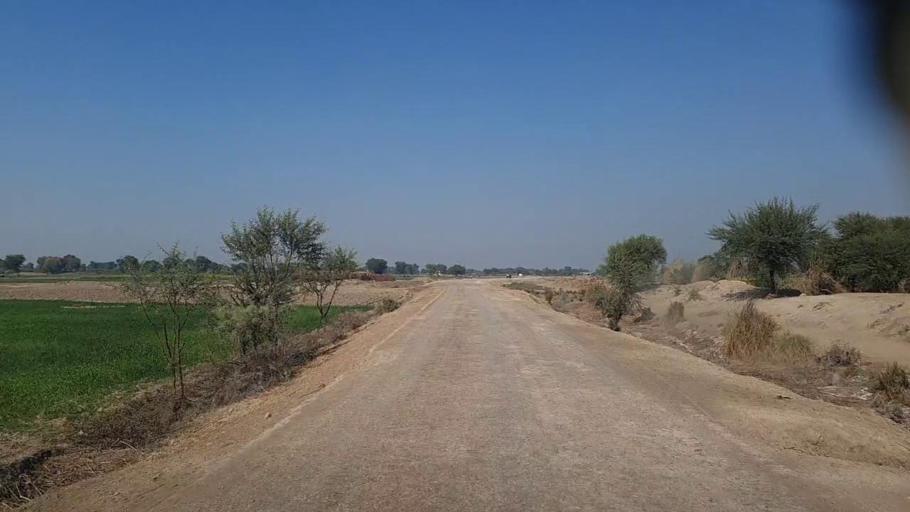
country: PK
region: Sindh
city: Khairpur
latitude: 27.9873
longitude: 69.8485
